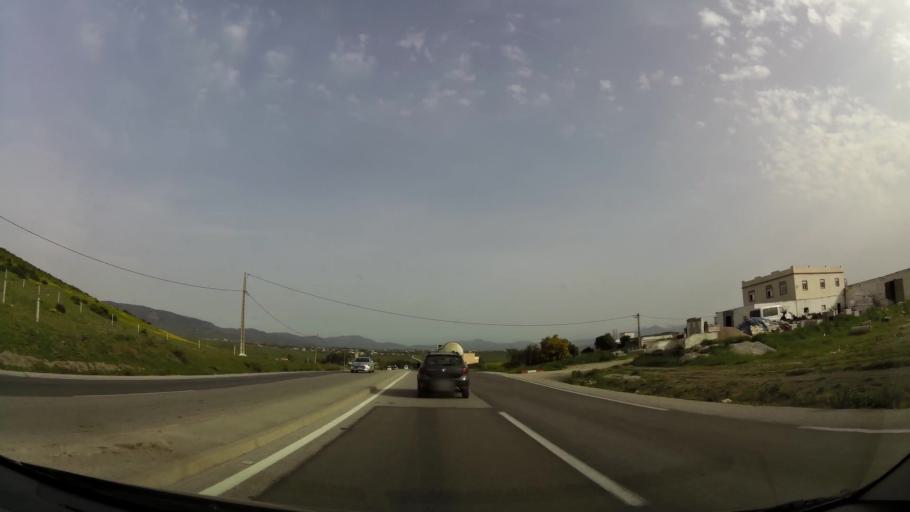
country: MA
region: Tanger-Tetouan
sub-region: Tanger-Assilah
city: Dar Chaoui
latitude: 35.6596
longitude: -5.6954
